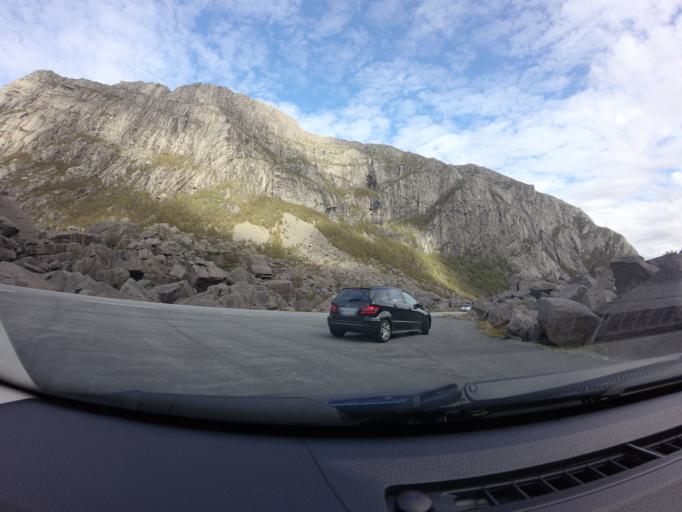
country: NO
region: Rogaland
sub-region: Forsand
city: Forsand
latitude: 58.7676
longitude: 6.2796
